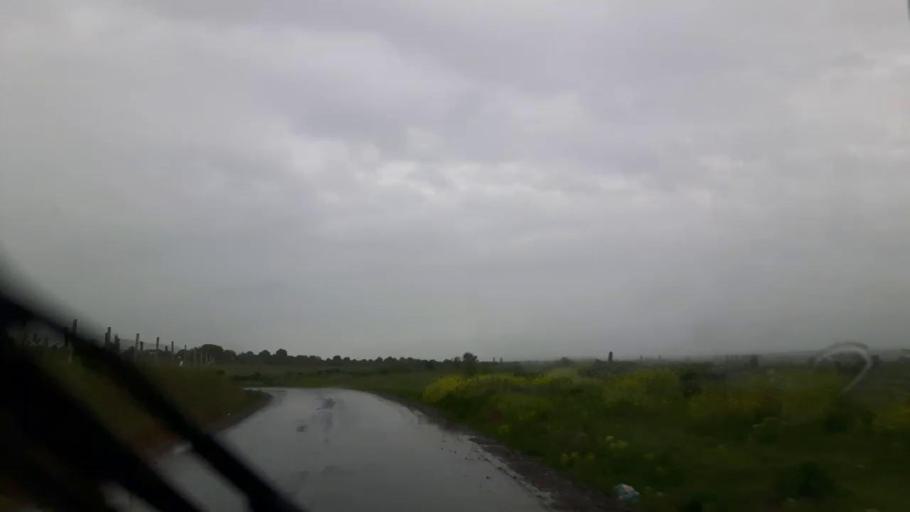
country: GE
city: Agara
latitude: 41.9823
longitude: 43.9504
